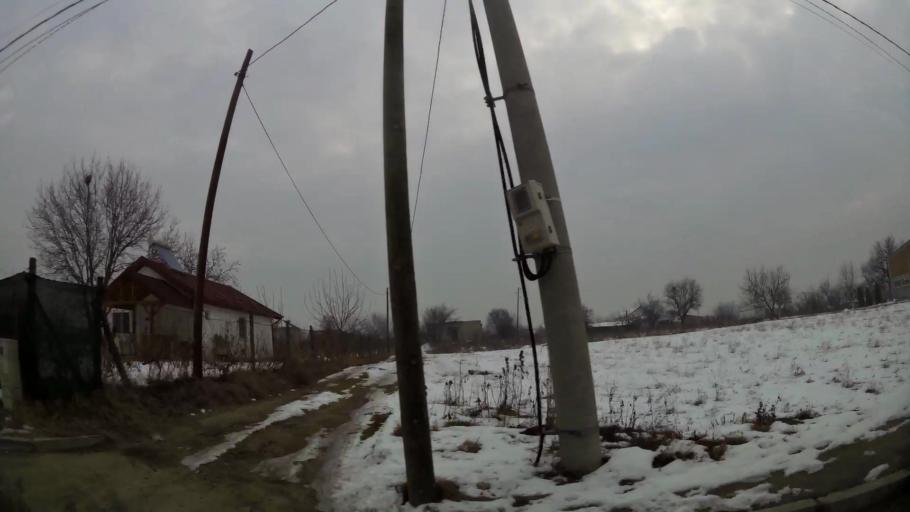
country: MK
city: Kondovo
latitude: 42.0335
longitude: 21.3434
